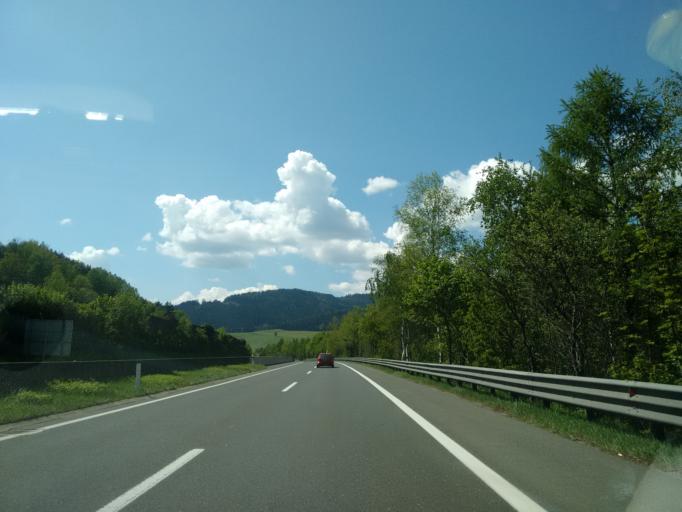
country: AT
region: Styria
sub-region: Politischer Bezirk Bruck-Muerzzuschlag
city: Oberaich
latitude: 47.4073
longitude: 15.2100
